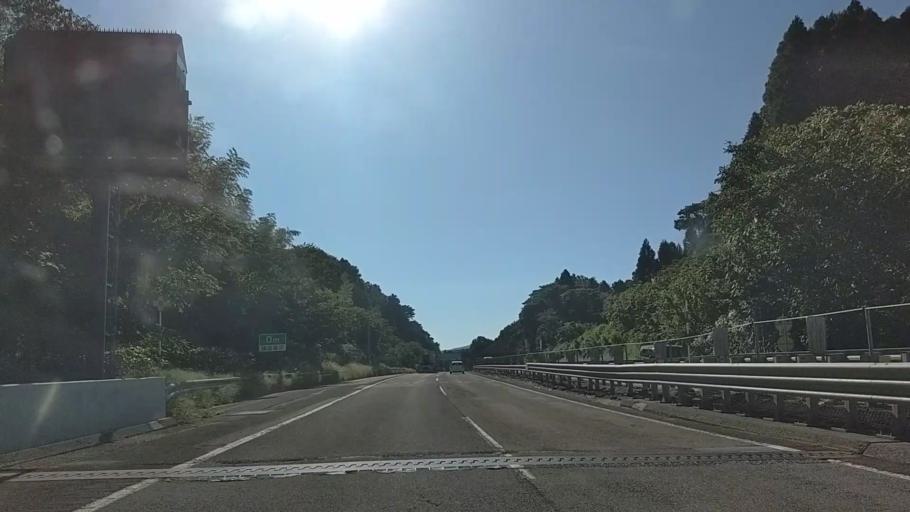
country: JP
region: Ishikawa
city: Tsubata
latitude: 36.6013
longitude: 136.7306
